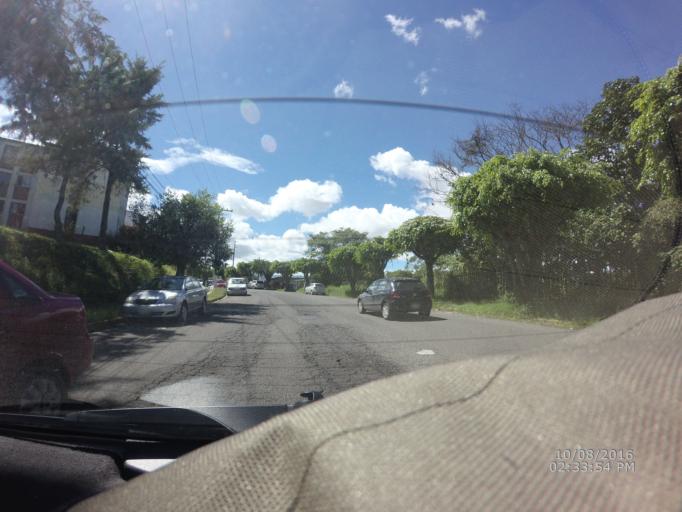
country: MX
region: Veracruz
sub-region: Xalapa
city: Lomas Verdes
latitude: 19.5134
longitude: -96.9009
